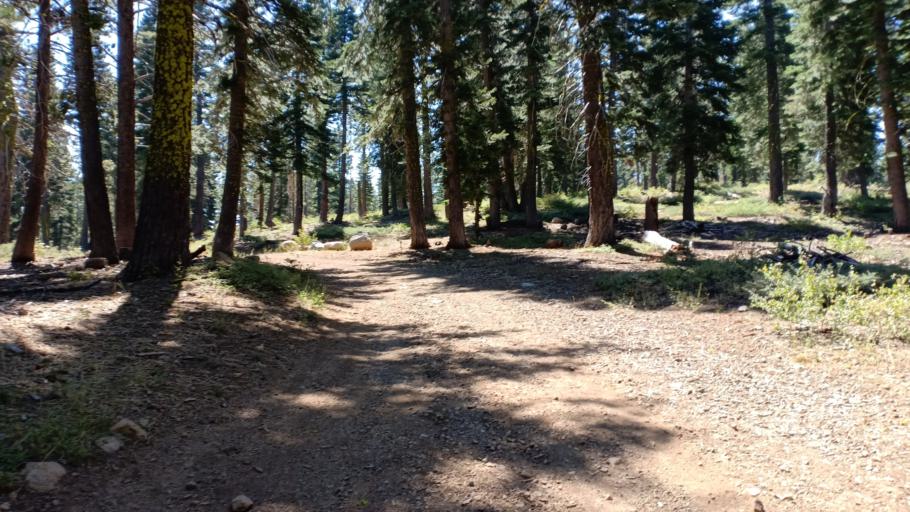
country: US
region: California
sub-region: Placer County
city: Sunnyside-Tahoe City
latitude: 39.1471
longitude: -120.1772
